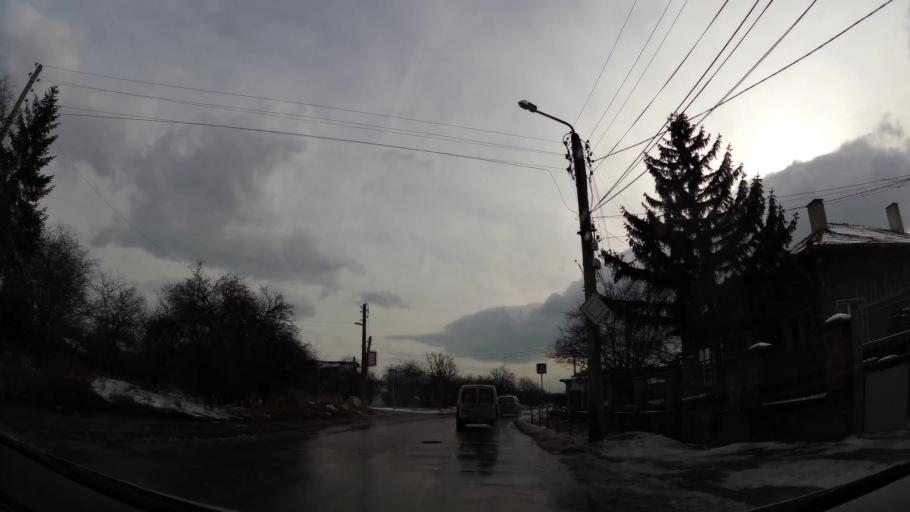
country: BG
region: Sofia-Capital
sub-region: Stolichna Obshtina
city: Sofia
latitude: 42.7015
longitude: 23.3873
